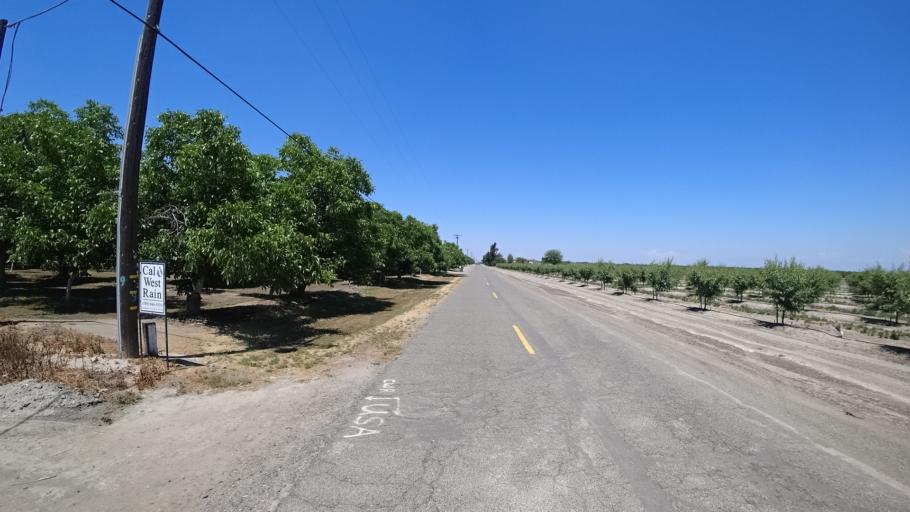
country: US
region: California
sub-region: Kings County
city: Lucerne
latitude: 36.4094
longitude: -119.6189
